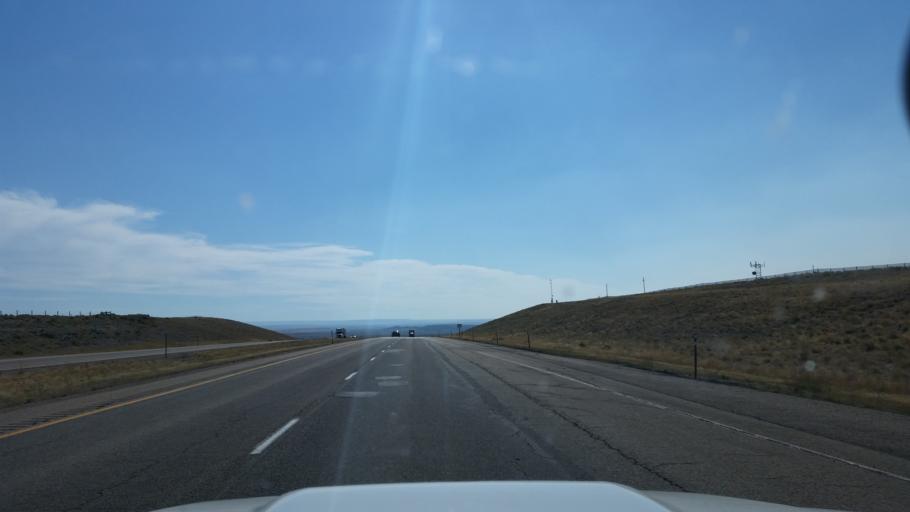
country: US
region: Wyoming
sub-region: Uinta County
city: Lyman
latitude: 41.4308
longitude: -110.1159
